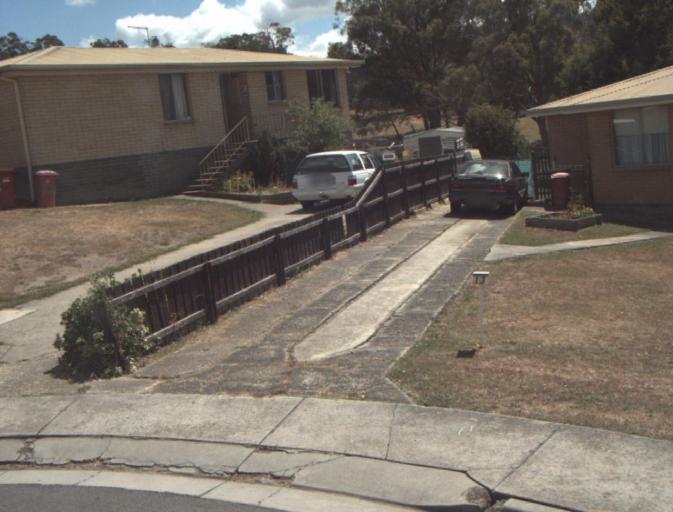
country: AU
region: Tasmania
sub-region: Launceston
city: Newstead
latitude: -41.4099
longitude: 147.1699
